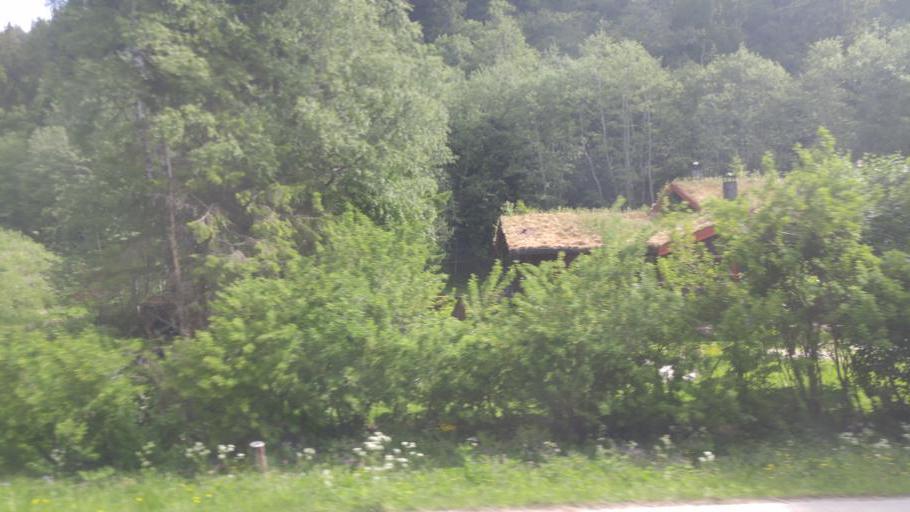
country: NO
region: Sor-Trondelag
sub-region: Midtre Gauldal
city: Storen
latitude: 63.0380
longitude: 10.2977
